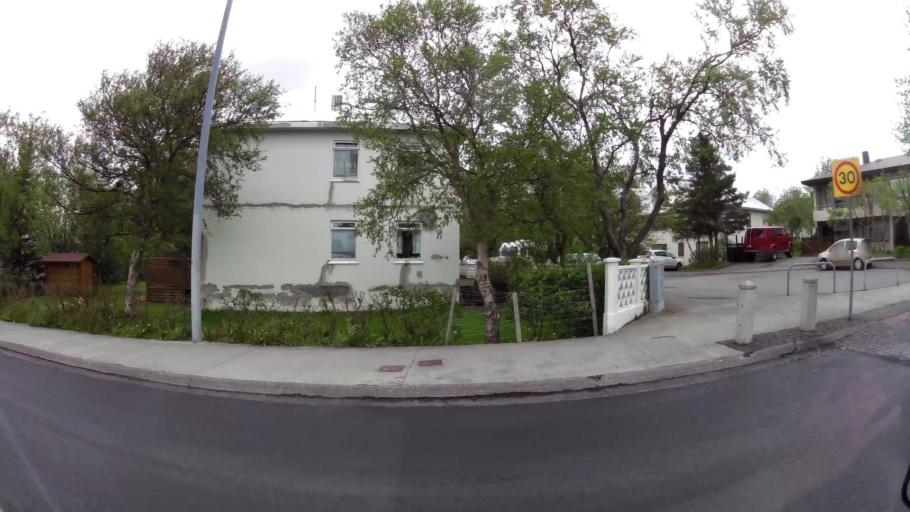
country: IS
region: Capital Region
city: Reykjavik
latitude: 64.1225
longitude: -21.8687
